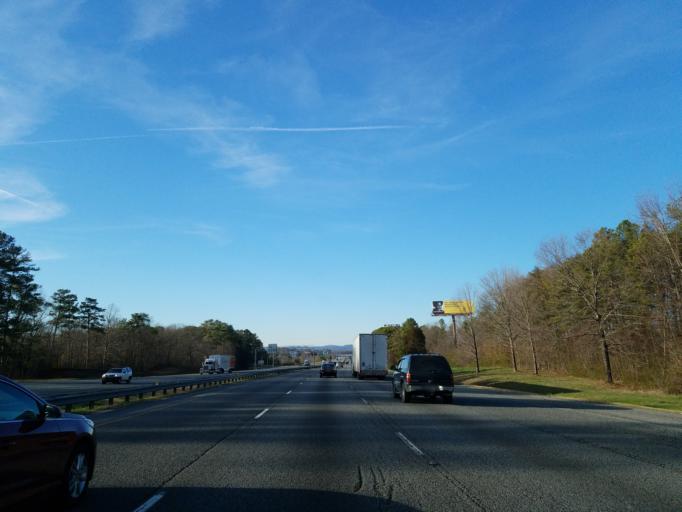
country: US
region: Georgia
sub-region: Gordon County
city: Calhoun
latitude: 34.5603
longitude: -84.9390
